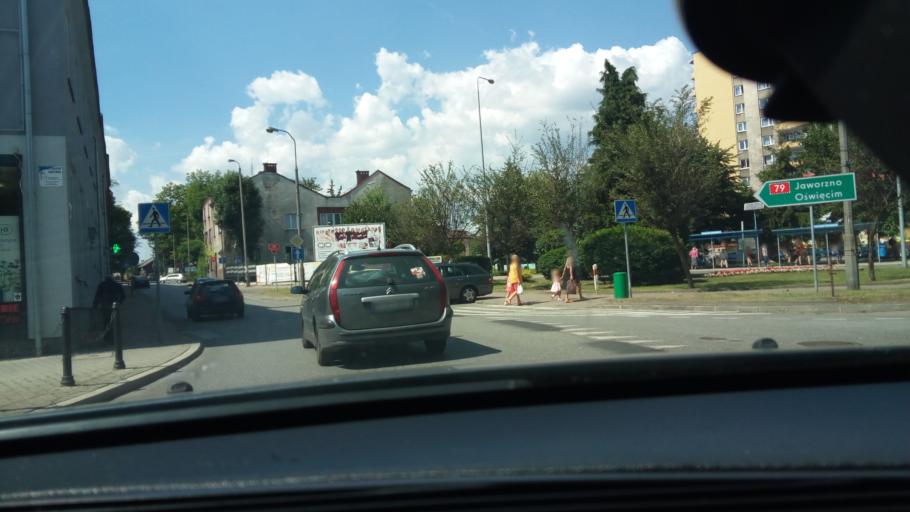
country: PL
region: Lesser Poland Voivodeship
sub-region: Powiat chrzanowski
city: Chrzanow
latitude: 50.1436
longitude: 19.4052
